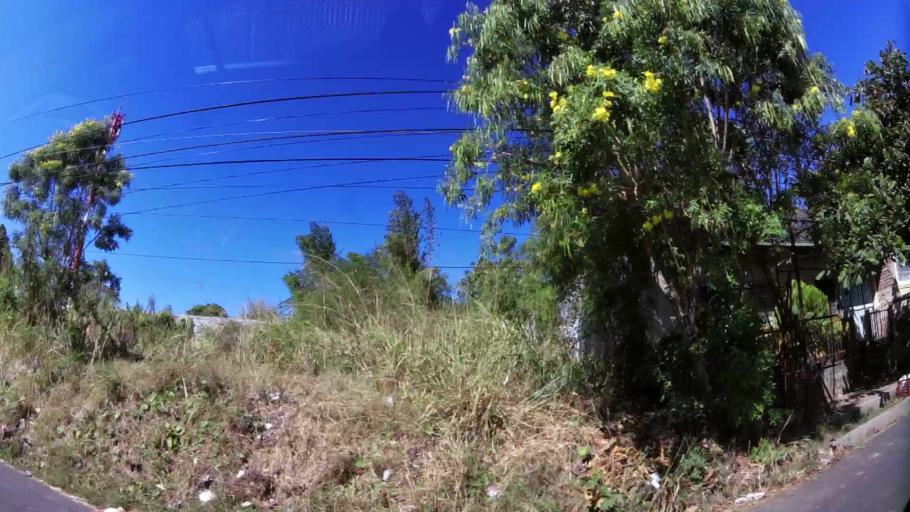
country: SV
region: Ahuachapan
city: Ahuachapan
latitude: 13.9186
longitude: -89.8438
